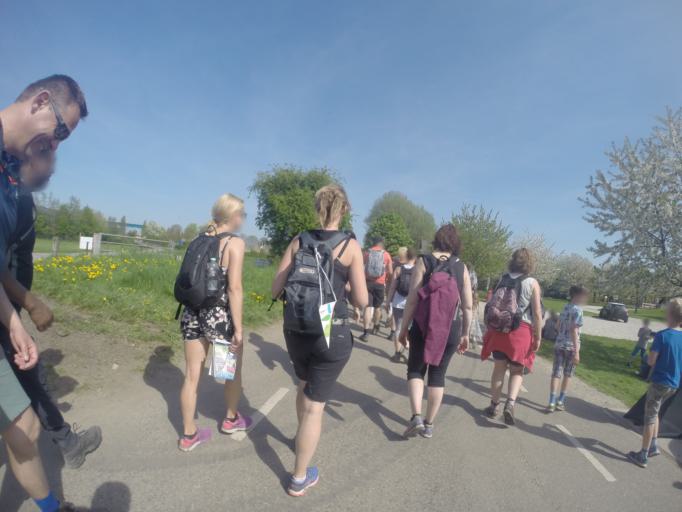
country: NL
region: Gelderland
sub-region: Gemeente Geldermalsen
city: Geldermalsen
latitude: 51.8815
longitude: 5.2620
